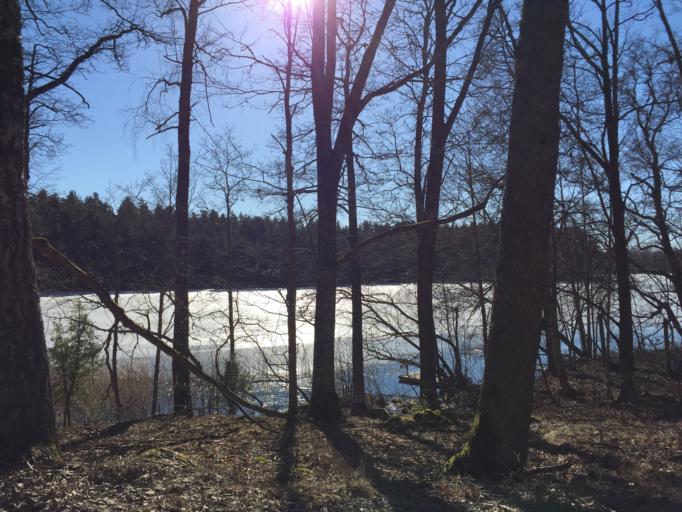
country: SE
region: OEstergoetland
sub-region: Finspangs Kommun
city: Finspang
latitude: 58.9014
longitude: 15.7314
